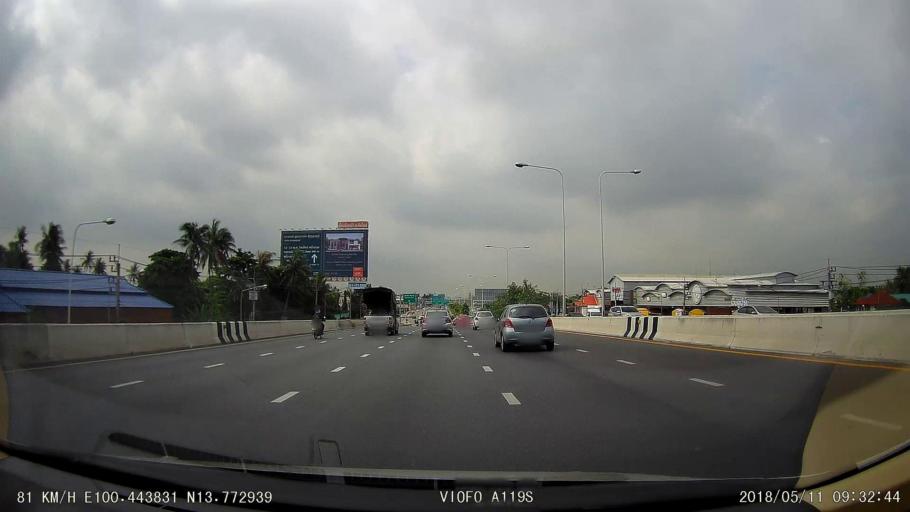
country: TH
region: Bangkok
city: Taling Chan
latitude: 13.7727
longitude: 100.4439
